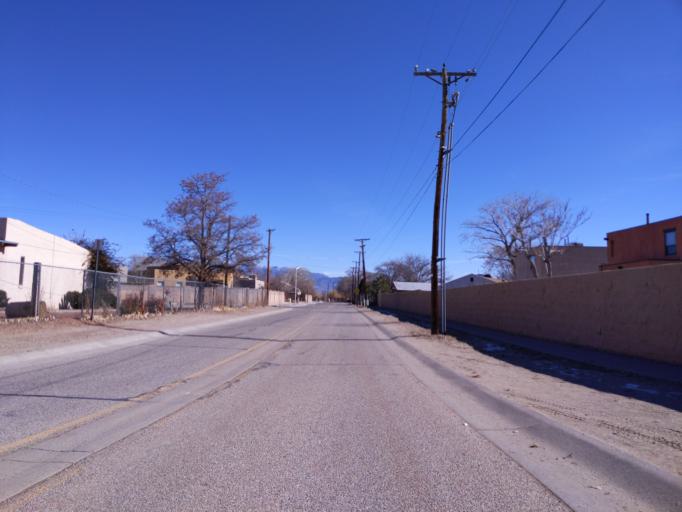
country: US
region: New Mexico
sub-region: Bernalillo County
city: Albuquerque
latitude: 35.0996
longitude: -106.6857
